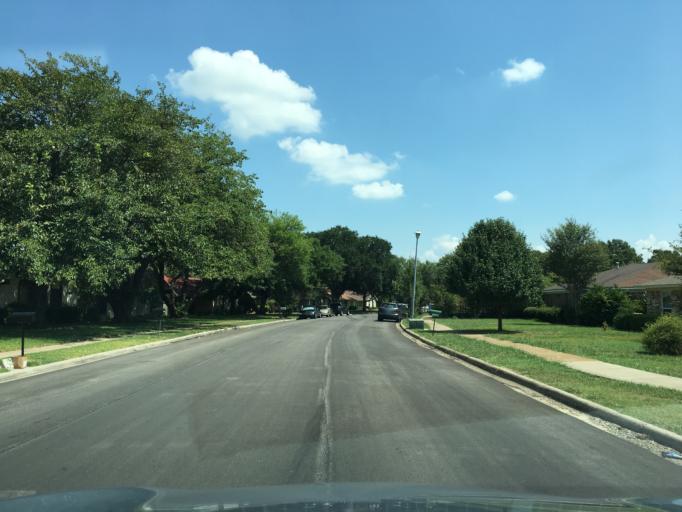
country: US
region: Texas
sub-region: Dallas County
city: Garland
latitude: 32.9387
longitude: -96.6603
